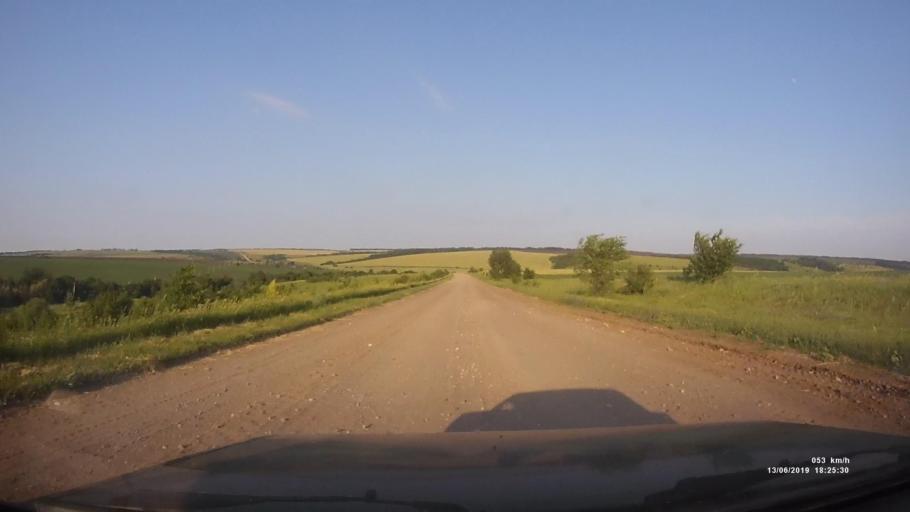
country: RU
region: Rostov
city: Kazanskaya
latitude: 49.8509
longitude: 41.3023
